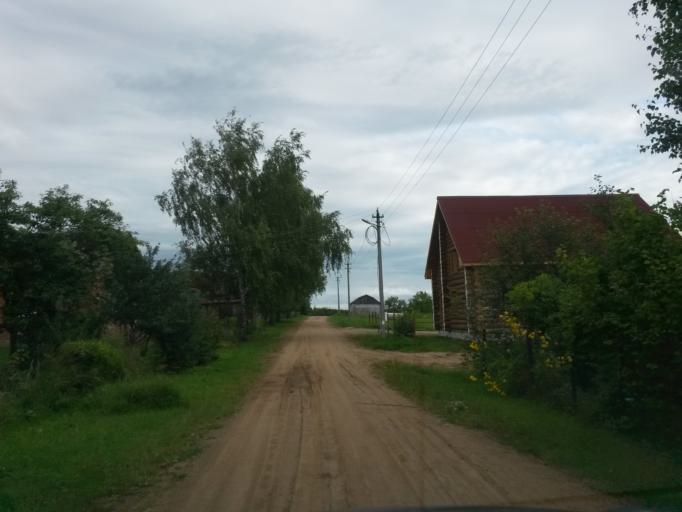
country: RU
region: Jaroslavl
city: Gavrilov-Yam
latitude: 57.3088
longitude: 39.9514
